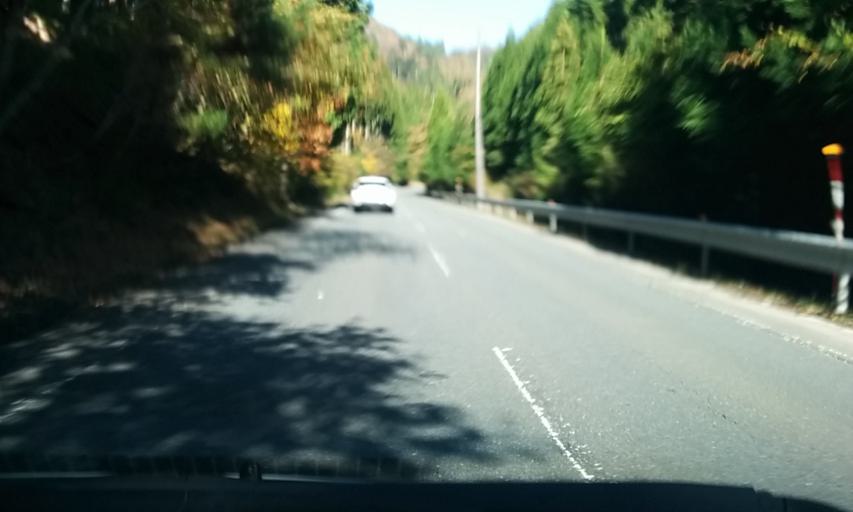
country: JP
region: Kyoto
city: Kameoka
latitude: 35.2180
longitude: 135.5697
